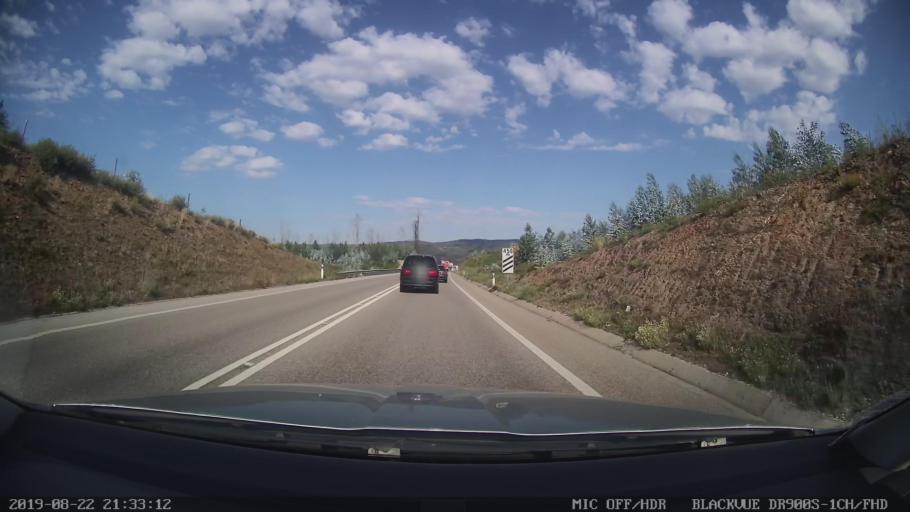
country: PT
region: Leiria
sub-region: Pedrogao Grande
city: Pedrogao Grande
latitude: 39.9261
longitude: -8.1746
